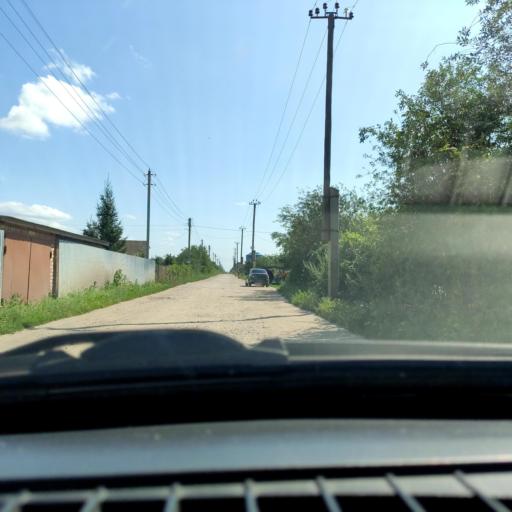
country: RU
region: Samara
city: Tol'yatti
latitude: 53.7308
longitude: 49.3955
